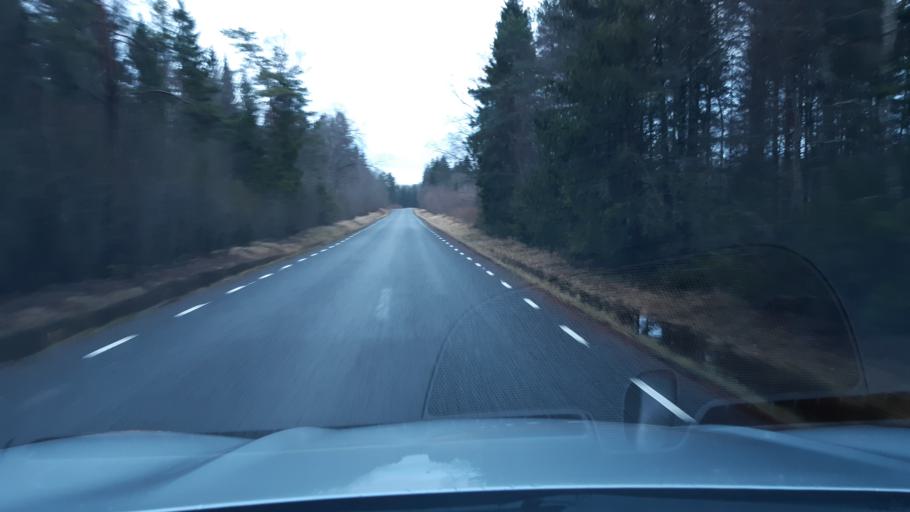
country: EE
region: Harju
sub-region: Saku vald
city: Saku
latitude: 59.1840
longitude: 24.6079
